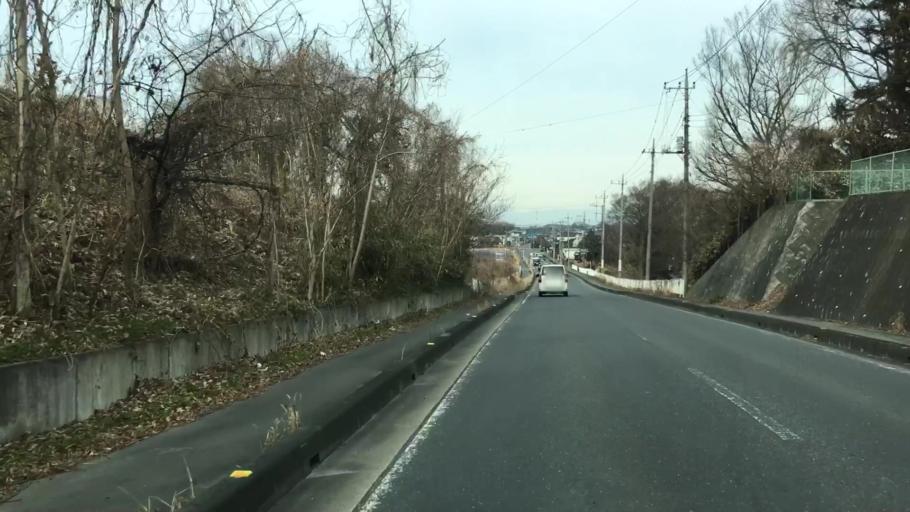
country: JP
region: Saitama
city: Kumagaya
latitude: 36.1251
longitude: 139.3248
